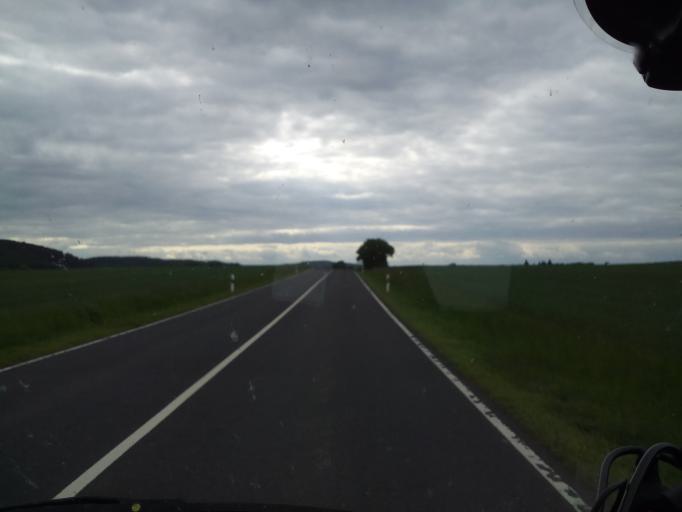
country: DE
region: Thuringia
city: Veilsdorf
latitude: 50.4177
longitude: 10.7877
